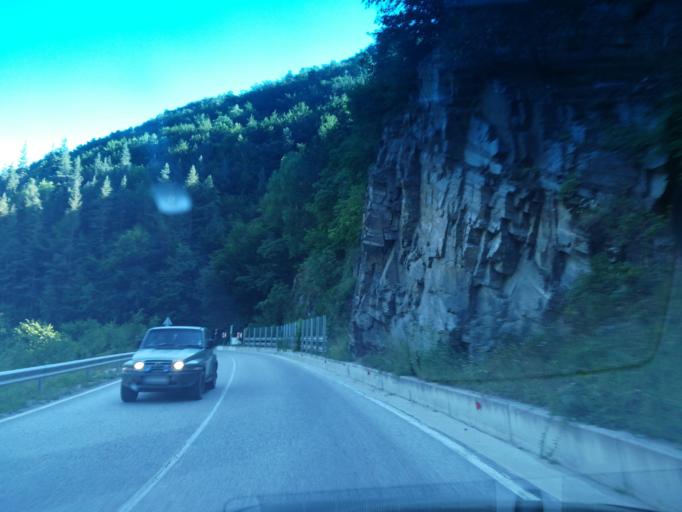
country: BG
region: Smolyan
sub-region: Obshtina Chepelare
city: Chepelare
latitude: 41.7984
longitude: 24.7090
